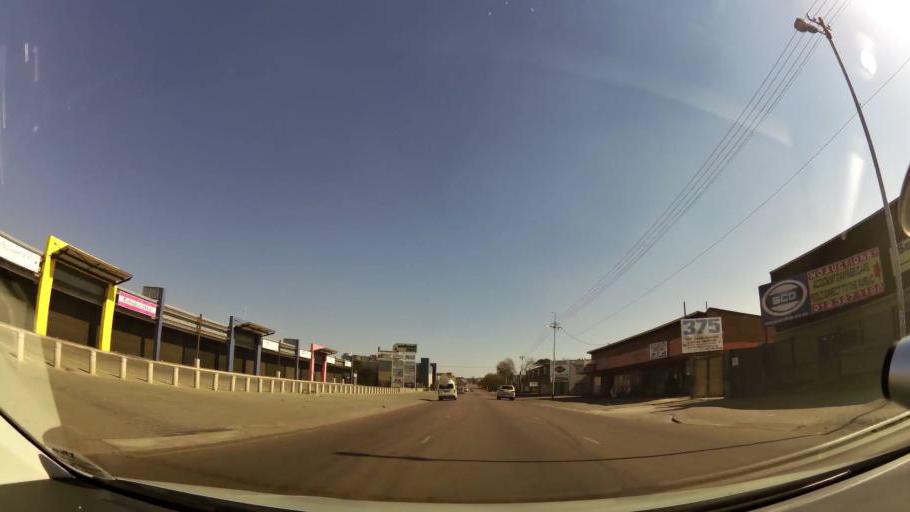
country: ZA
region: Gauteng
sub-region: City of Tshwane Metropolitan Municipality
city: Pretoria
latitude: -25.7548
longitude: 28.1590
